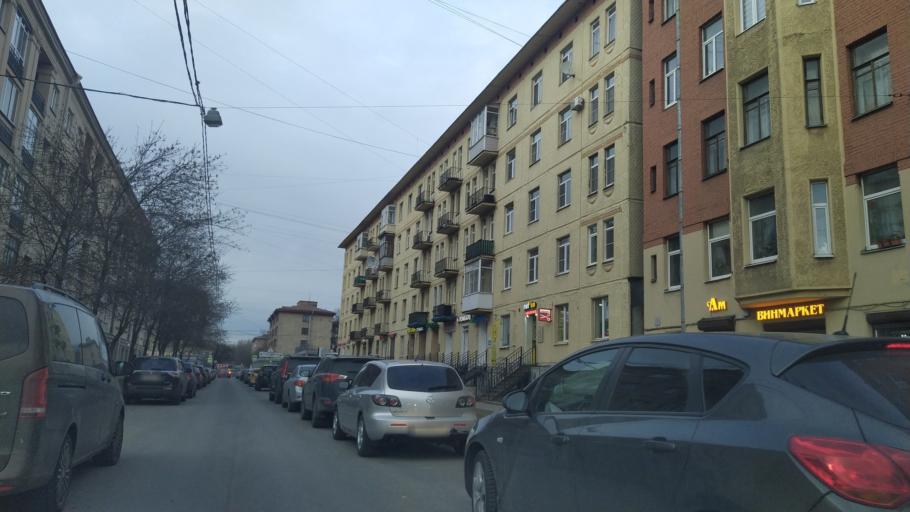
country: RU
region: Leningrad
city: Sampsonievskiy
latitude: 59.9841
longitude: 30.3461
